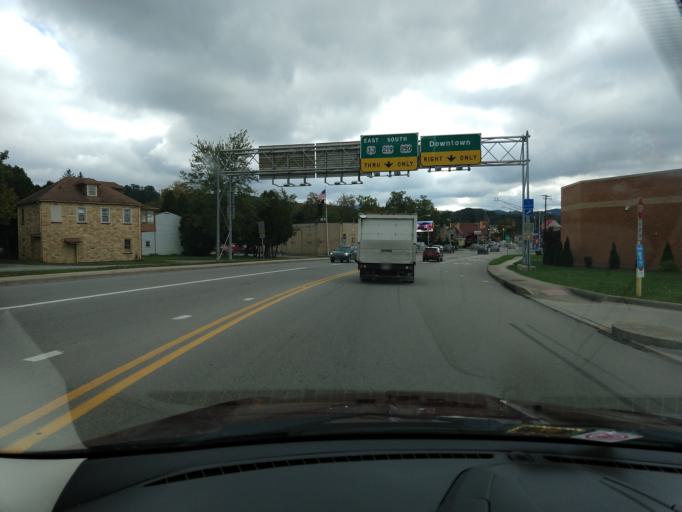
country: US
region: West Virginia
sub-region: Randolph County
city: Elkins
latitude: 38.9293
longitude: -79.8501
